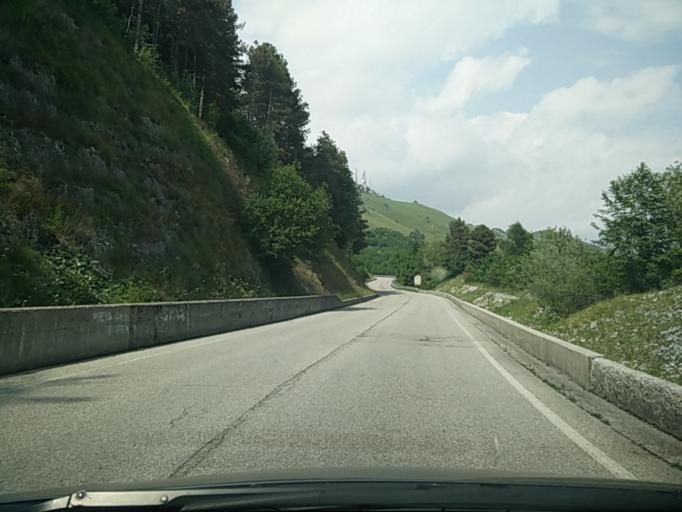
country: IT
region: Friuli Venezia Giulia
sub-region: Provincia di Pordenone
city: Budoia
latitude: 46.0804
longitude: 12.5297
